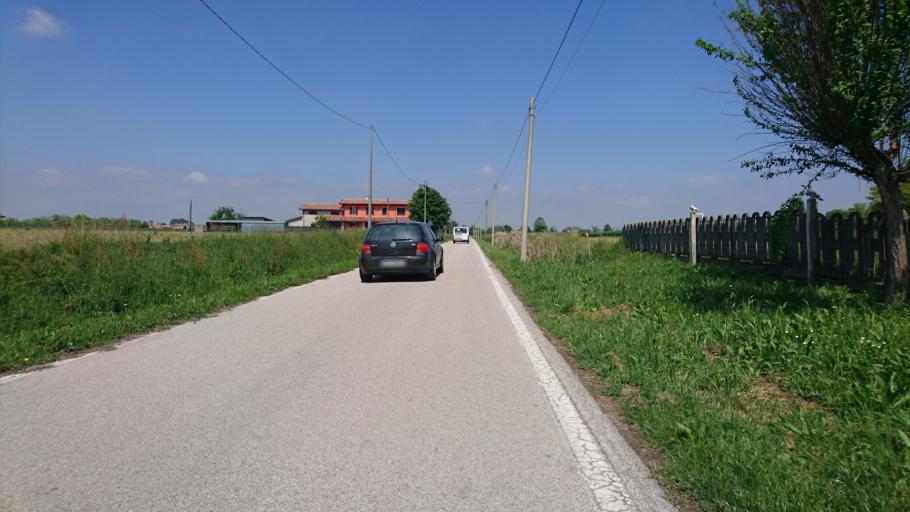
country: IT
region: Veneto
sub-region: Provincia di Padova
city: Bertipaglia
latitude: 45.3205
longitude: 11.8900
